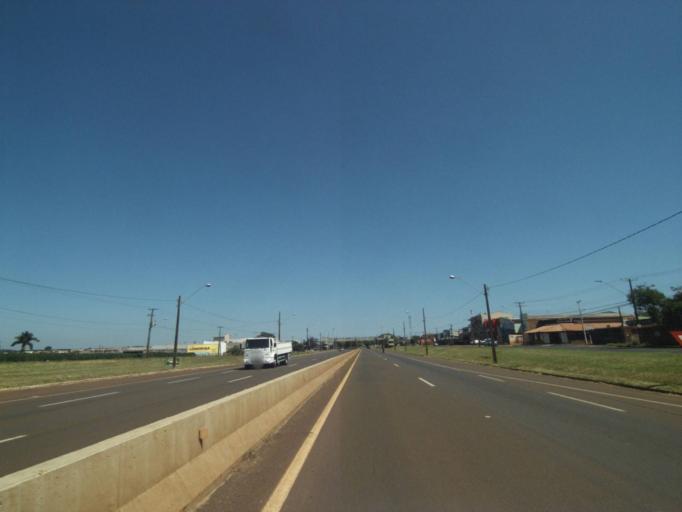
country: BR
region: Parana
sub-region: Londrina
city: Londrina
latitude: -23.3655
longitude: -51.1440
